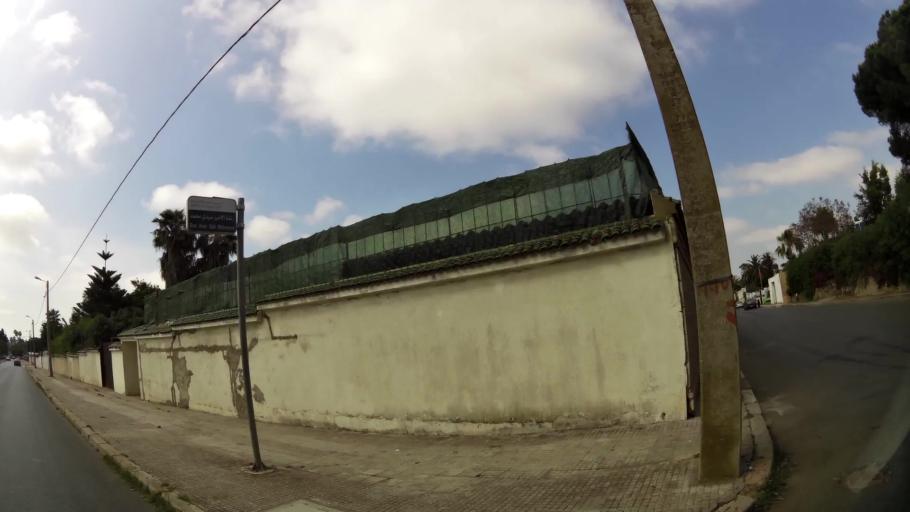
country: MA
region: Rabat-Sale-Zemmour-Zaer
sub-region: Rabat
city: Rabat
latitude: 33.9743
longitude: -6.8452
